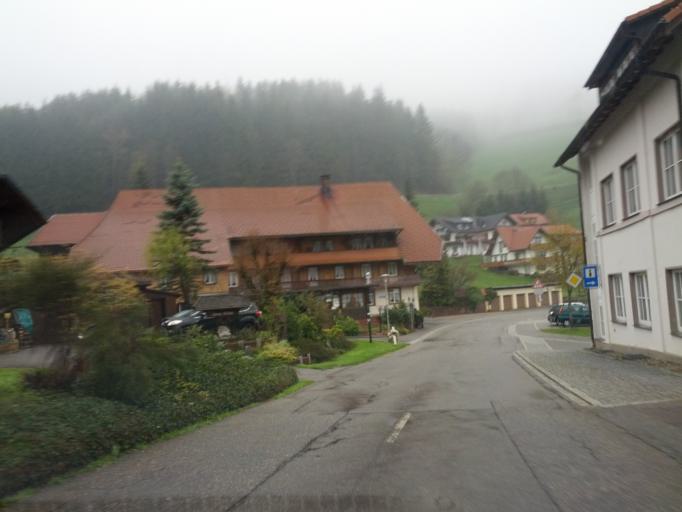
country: DE
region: Baden-Wuerttemberg
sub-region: Freiburg Region
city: Wieden
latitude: 47.8406
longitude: 7.8808
